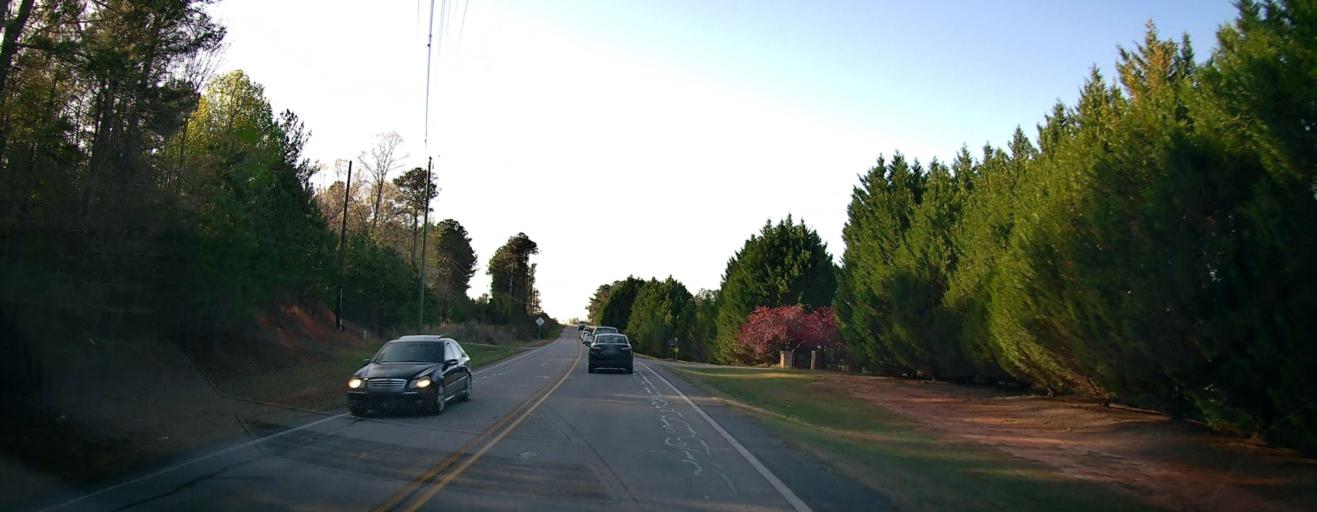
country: US
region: Georgia
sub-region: Newton County
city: Oakwood
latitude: 33.4376
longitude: -83.8982
